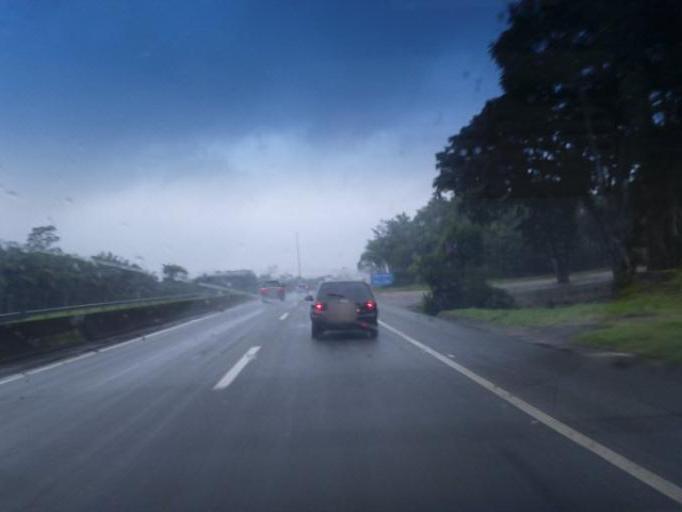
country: BR
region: Santa Catarina
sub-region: Joinville
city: Joinville
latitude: -25.9816
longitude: -48.8865
